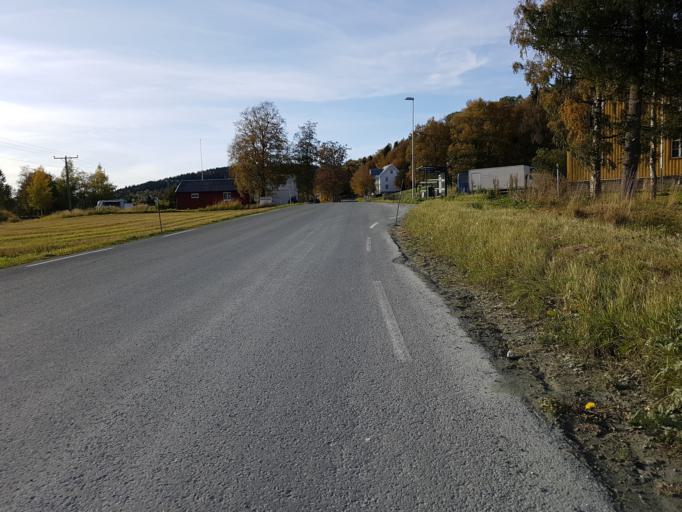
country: NO
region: Sor-Trondelag
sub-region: Klaebu
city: Klaebu
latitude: 63.3494
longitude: 10.4983
